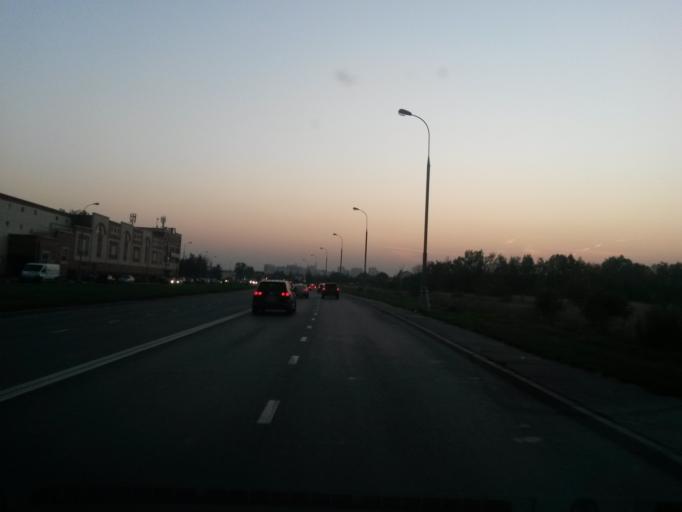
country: RU
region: Moskovskaya
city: Kommunarka
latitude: 55.5478
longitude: 37.5186
